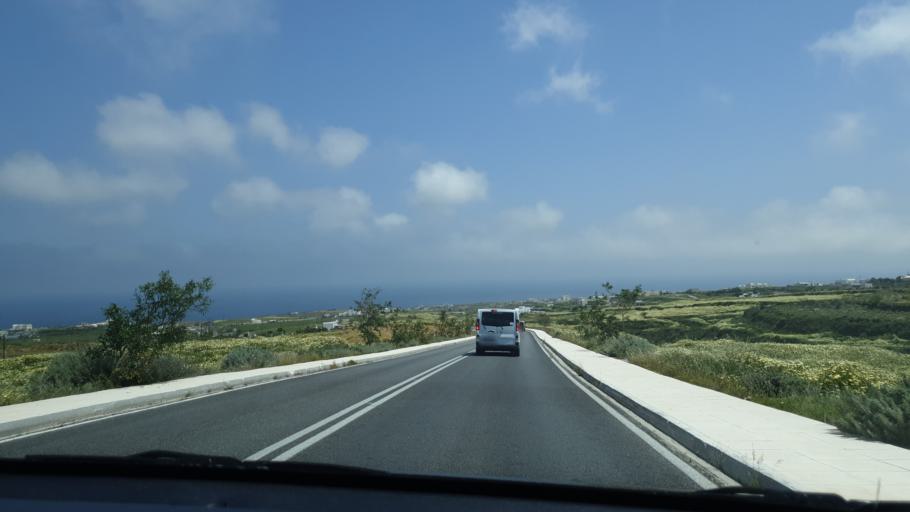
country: GR
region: South Aegean
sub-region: Nomos Kykladon
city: Fira
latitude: 36.4169
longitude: 25.4429
